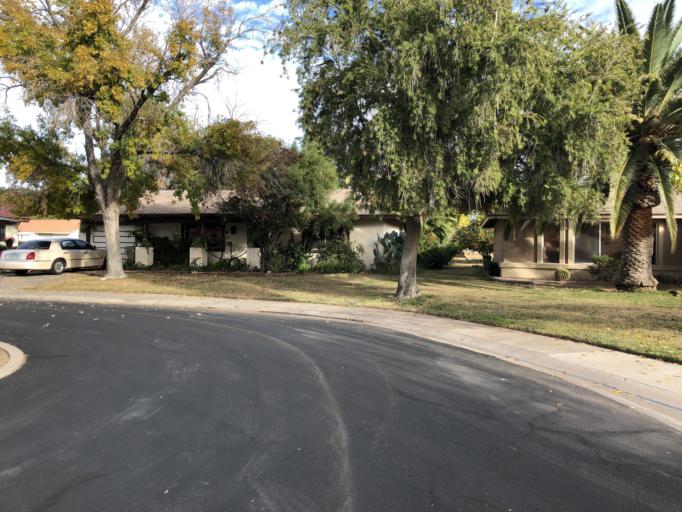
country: US
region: Arizona
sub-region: Maricopa County
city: Gilbert
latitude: 33.4035
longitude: -111.6905
